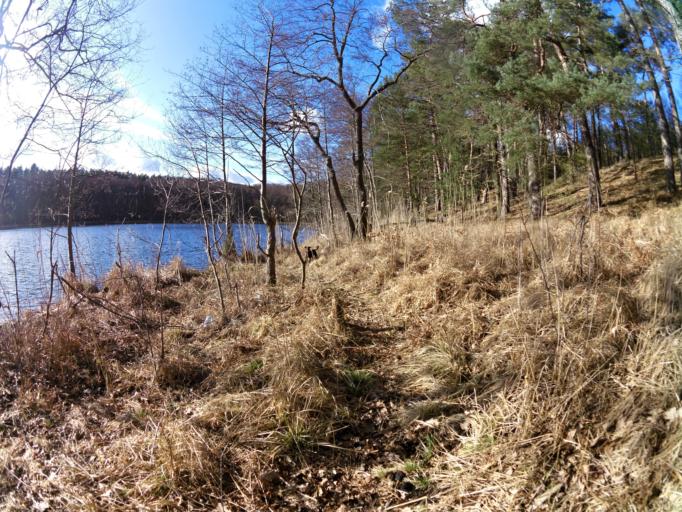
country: PL
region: West Pomeranian Voivodeship
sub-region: Powiat mysliborski
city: Debno
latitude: 52.7767
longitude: 14.7365
